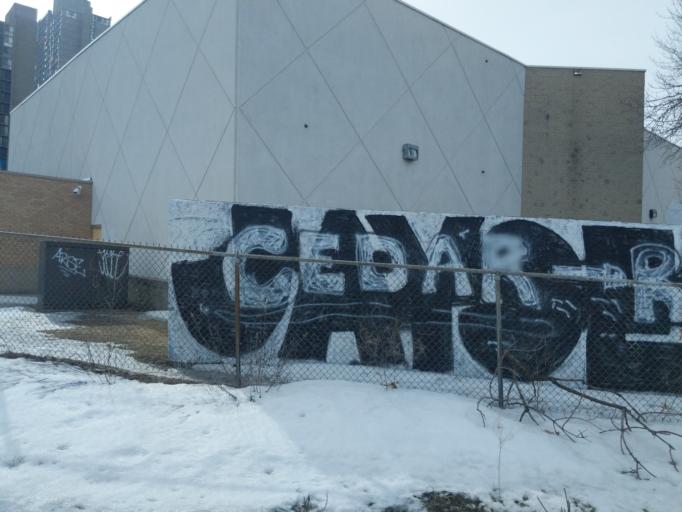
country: US
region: Minnesota
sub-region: Hennepin County
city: Minneapolis
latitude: 44.9710
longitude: -93.2507
